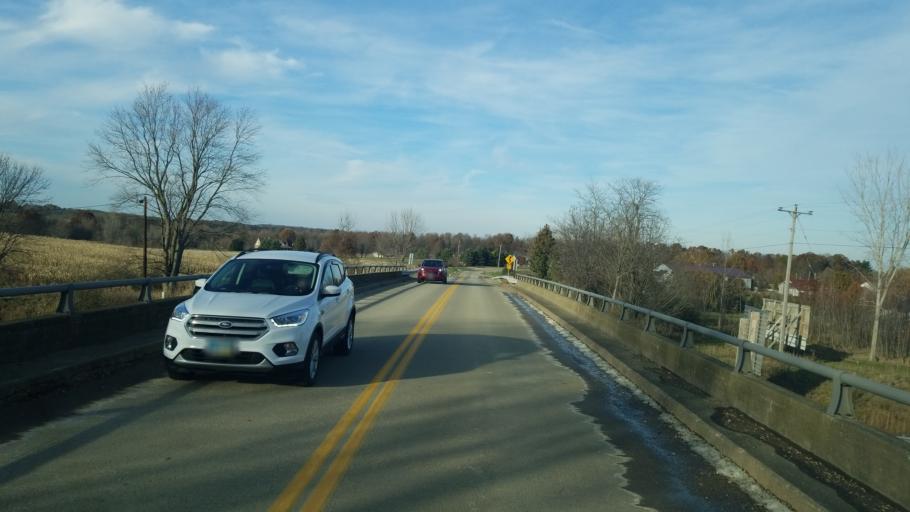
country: US
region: Ohio
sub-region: Ashland County
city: Ashland
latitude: 40.7843
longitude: -82.2555
